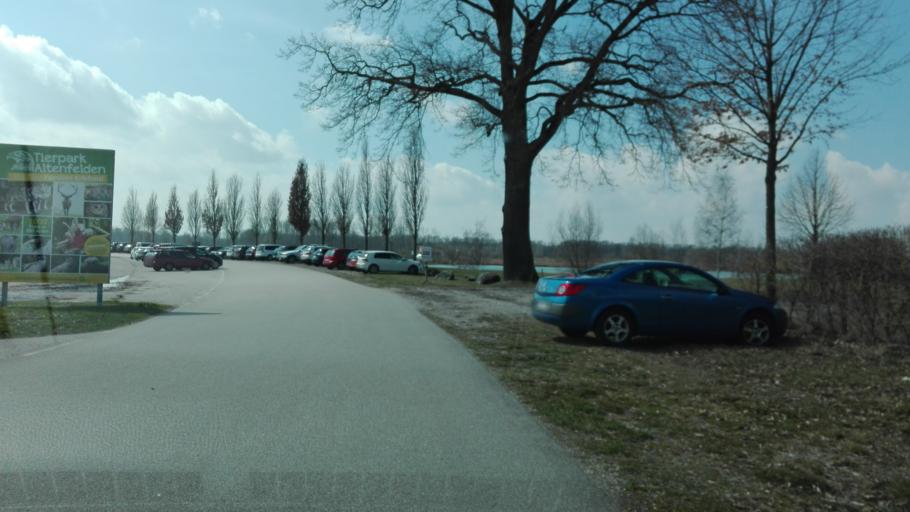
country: AT
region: Upper Austria
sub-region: Politischer Bezirk Urfahr-Umgebung
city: Feldkirchen an der Donau
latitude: 48.3278
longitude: 14.0708
